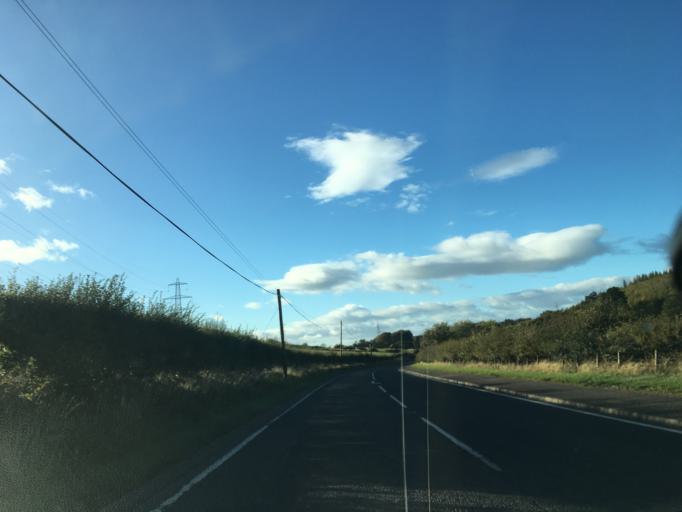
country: GB
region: Scotland
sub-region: Fife
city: Pathhead
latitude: 55.8461
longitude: -2.9306
